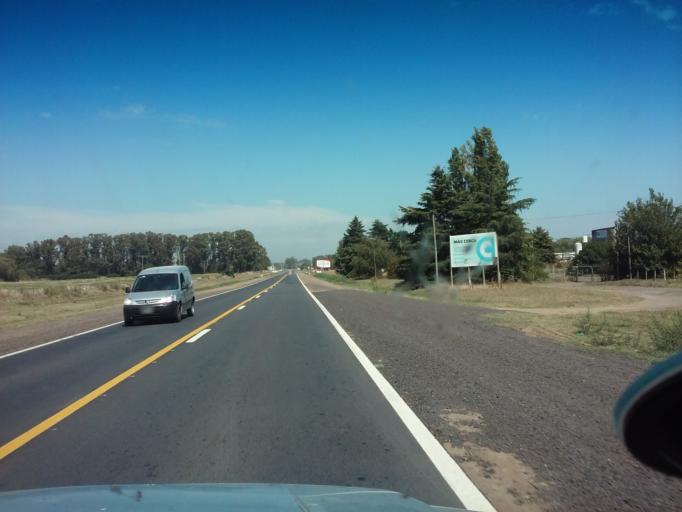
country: AR
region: Buenos Aires
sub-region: Partido de Nueve de Julio
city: Nueve de Julio
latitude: -35.4603
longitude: -60.8366
